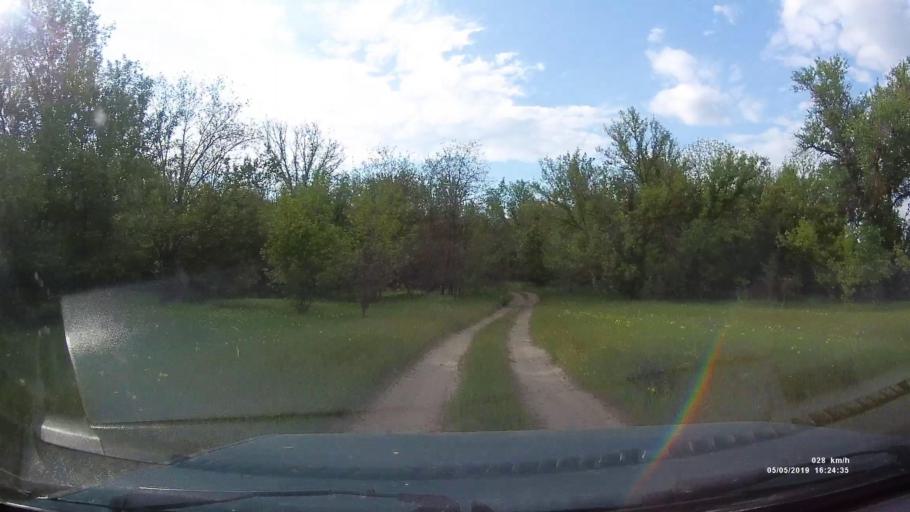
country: RU
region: Rostov
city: Konstantinovsk
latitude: 47.7599
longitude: 41.0254
